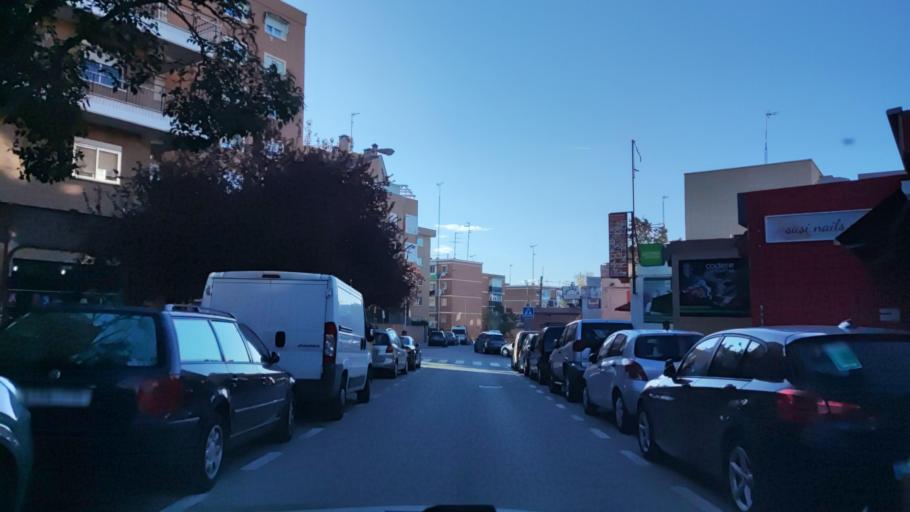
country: ES
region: Madrid
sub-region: Provincia de Madrid
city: Latina
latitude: 40.3977
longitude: -3.7713
